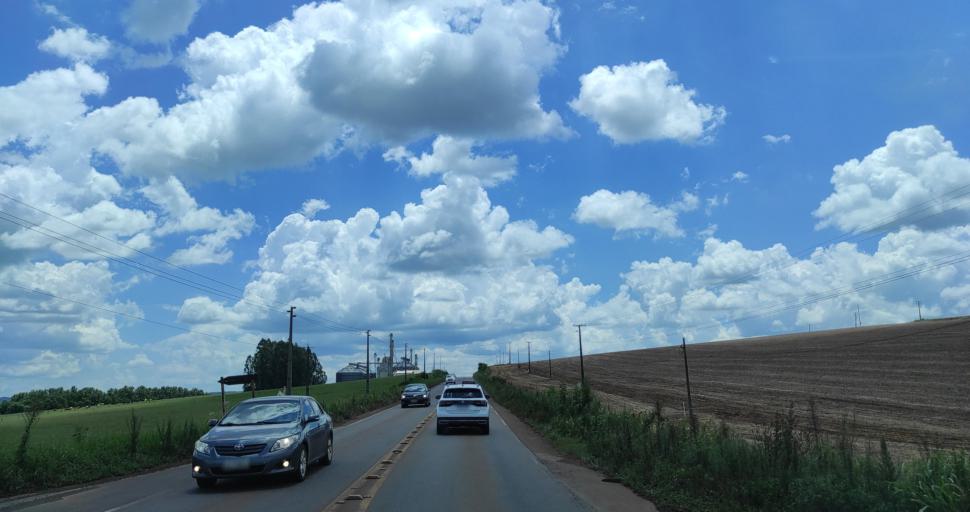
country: BR
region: Santa Catarina
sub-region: Xanxere
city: Xanxere
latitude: -26.7672
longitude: -52.4052
